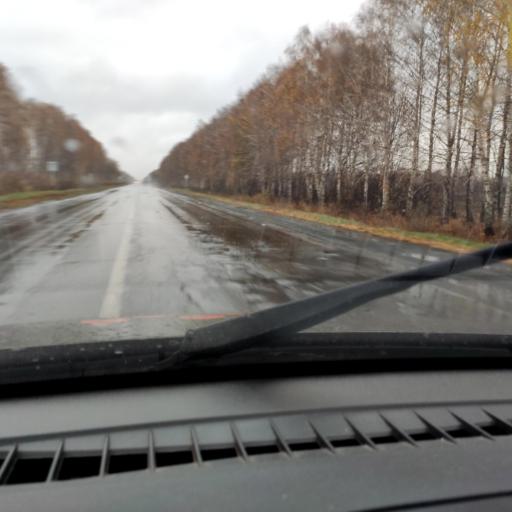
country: RU
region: Samara
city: Tol'yatti
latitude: 53.5923
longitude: 49.3281
